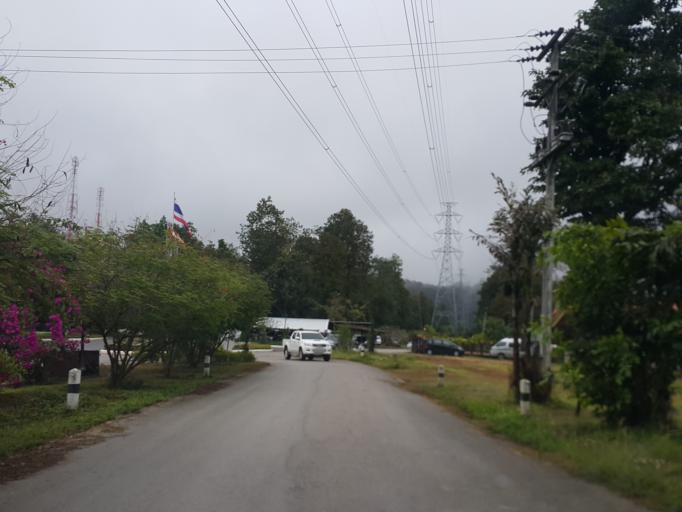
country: TH
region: Lampang
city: Hang Chat
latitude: 18.3577
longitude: 99.2419
